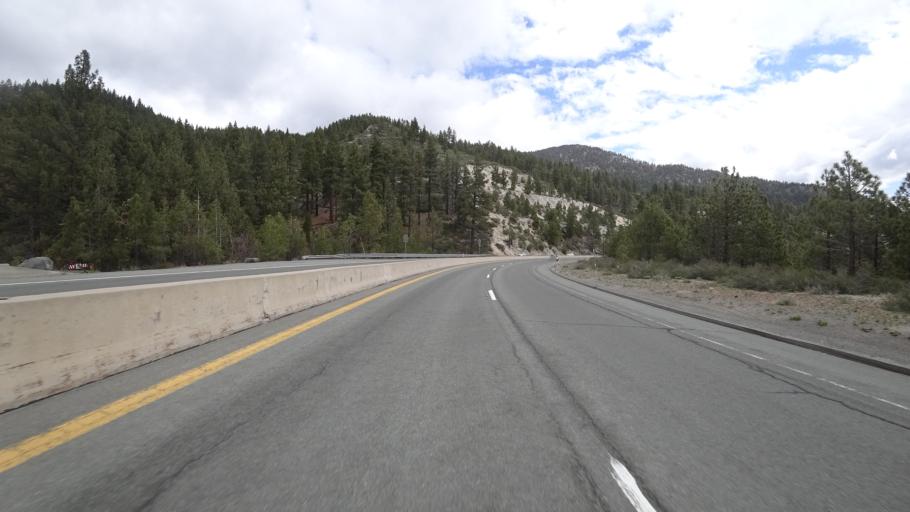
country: US
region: Nevada
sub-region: Douglas County
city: Indian Hills
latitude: 39.1155
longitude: -119.8868
